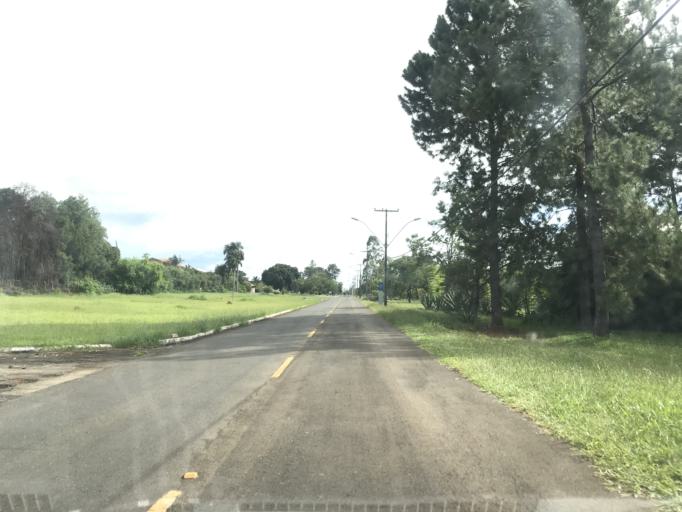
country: BR
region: Federal District
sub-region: Brasilia
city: Brasilia
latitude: -15.8908
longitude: -47.9183
